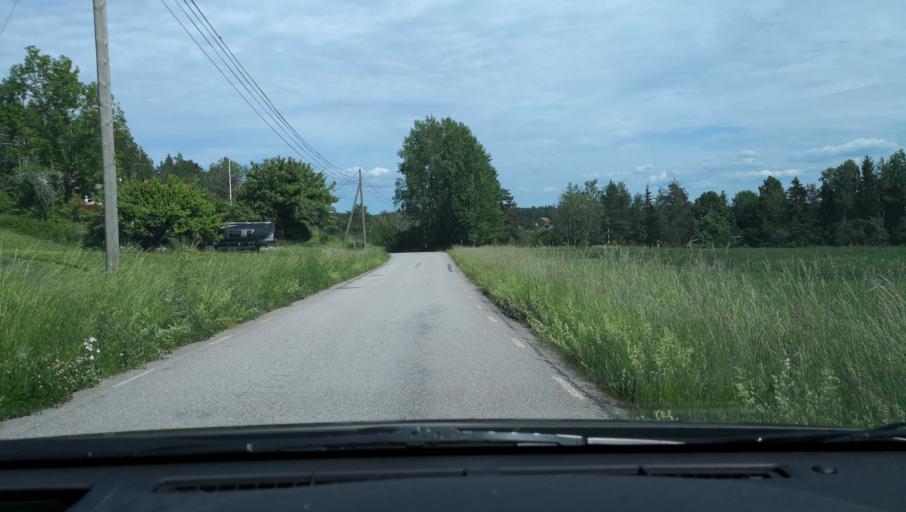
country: SE
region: Uppsala
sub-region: Uppsala Kommun
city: Alsike
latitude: 59.7047
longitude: 17.7133
